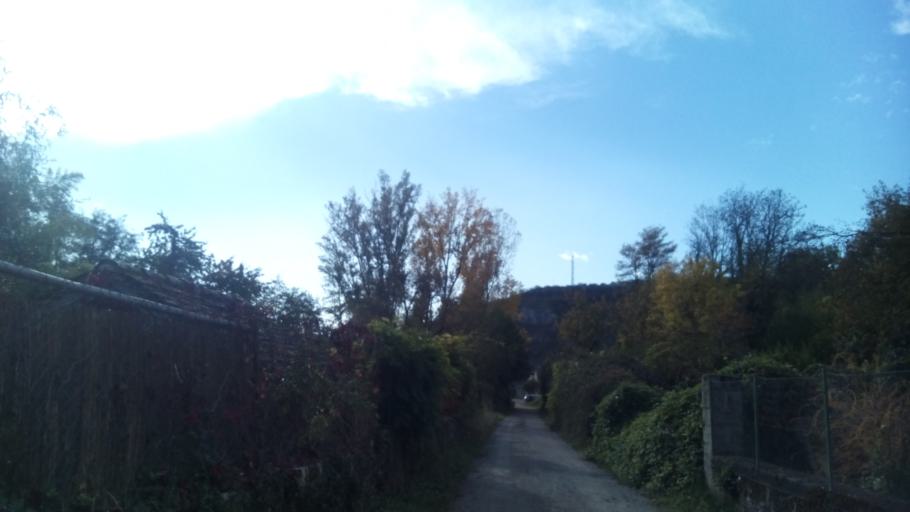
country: FR
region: Midi-Pyrenees
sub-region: Departement du Lot
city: Cajarc
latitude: 44.4842
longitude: 1.8470
